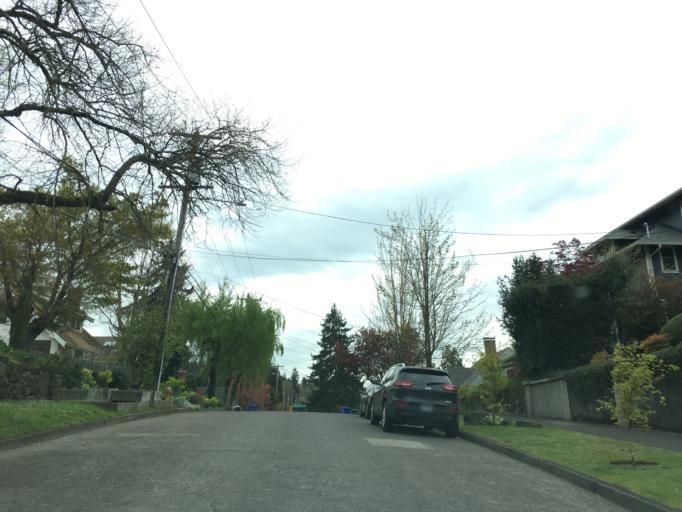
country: US
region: Oregon
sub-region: Multnomah County
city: Lents
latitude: 45.5257
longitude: -122.5996
